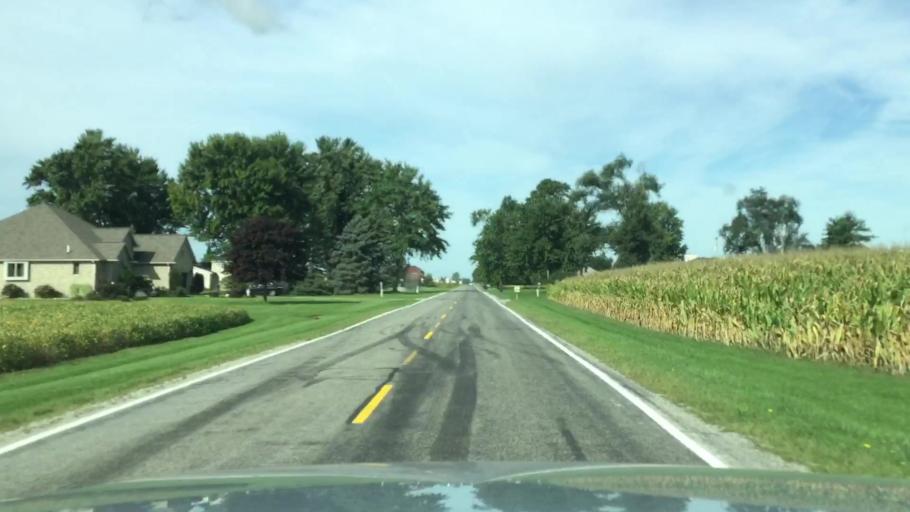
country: US
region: Michigan
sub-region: Genesee County
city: Montrose
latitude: 43.1471
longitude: -83.9493
